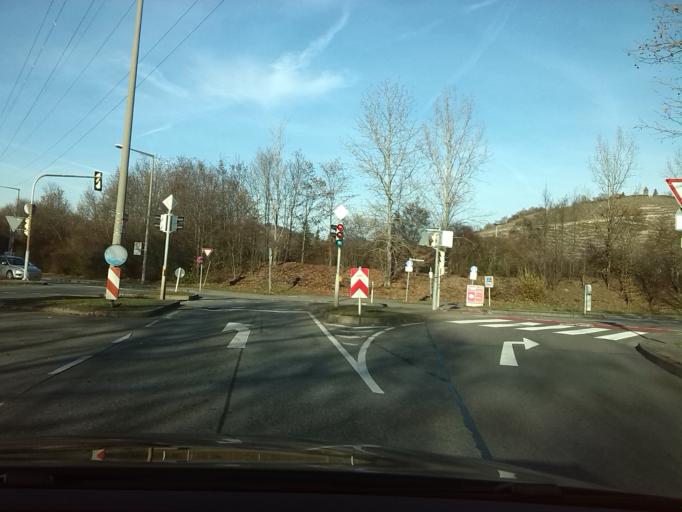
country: DE
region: Baden-Wuerttemberg
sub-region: Regierungsbezirk Stuttgart
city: Ostfildern
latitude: 48.7566
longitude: 9.2694
